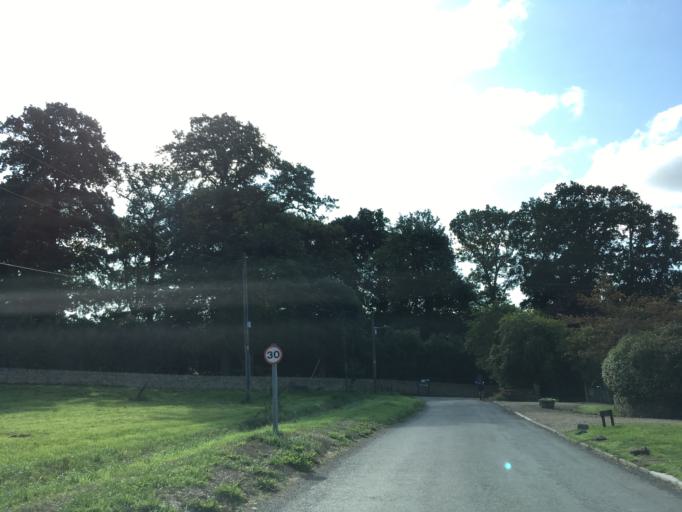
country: GB
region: England
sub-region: South Gloucestershire
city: Horton
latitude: 51.5239
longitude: -2.3565
